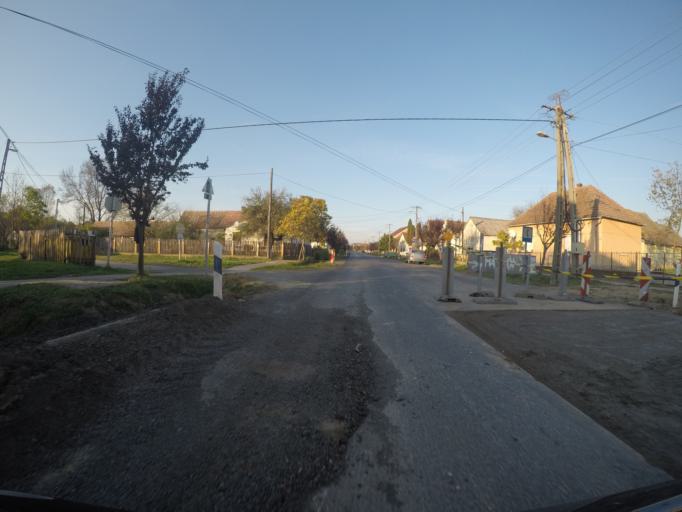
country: HU
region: Somogy
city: Barcs
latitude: 45.9821
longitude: 17.5899
